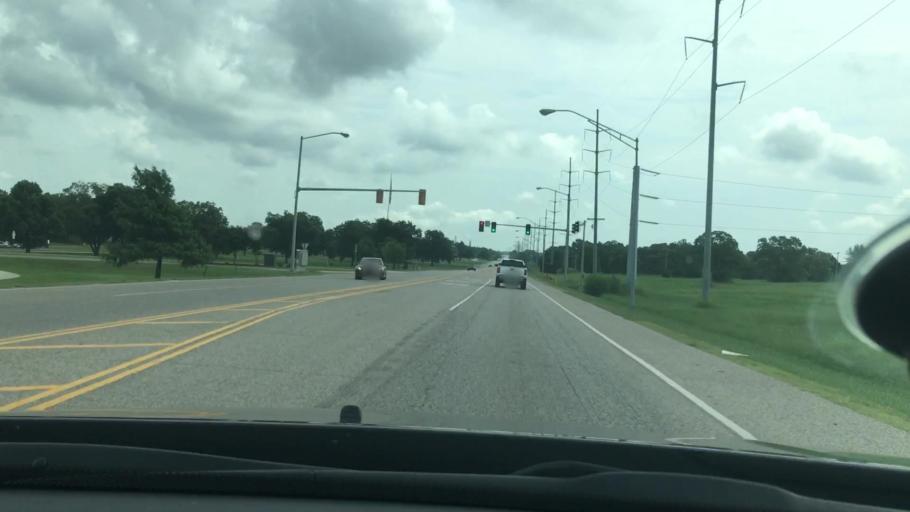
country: US
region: Oklahoma
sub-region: Carter County
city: Ardmore
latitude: 34.2028
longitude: -97.1362
